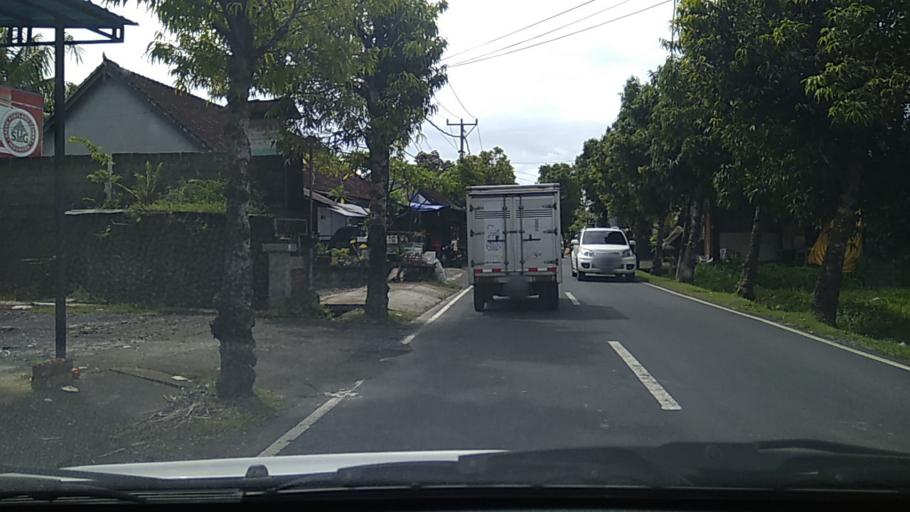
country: ID
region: Bali
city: Banjar Sedang
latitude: -8.5685
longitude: 115.2555
